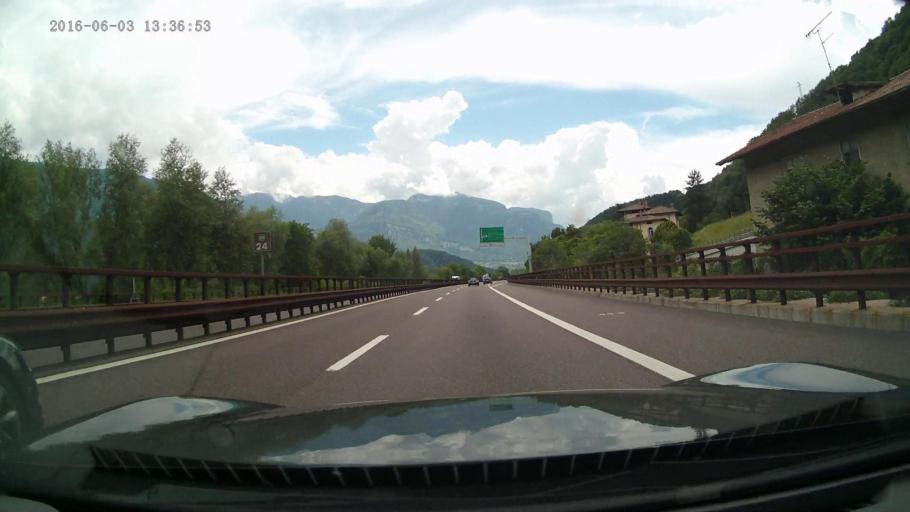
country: IT
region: Trentino-Alto Adige
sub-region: Bolzano
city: Ora
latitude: 46.3646
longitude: 11.2901
